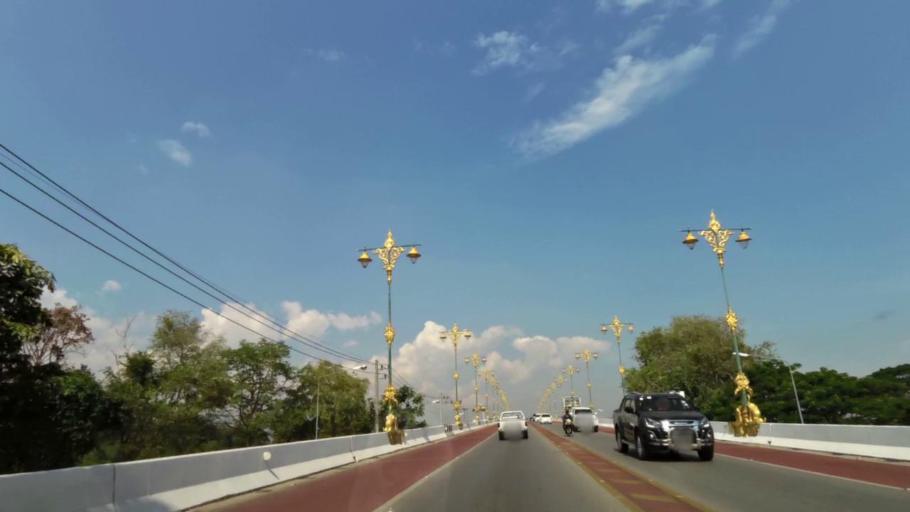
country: TH
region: Chiang Rai
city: Chiang Rai
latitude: 19.9164
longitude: 99.8326
